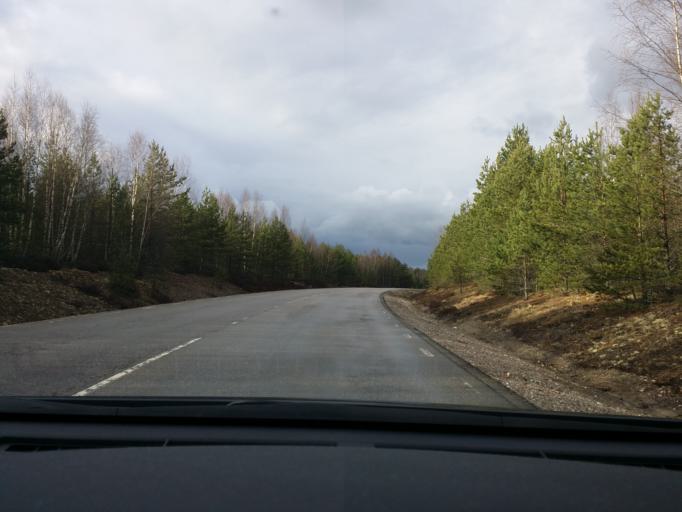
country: SE
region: Soedermanland
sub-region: Eskilstuna Kommun
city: Arla
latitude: 59.3212
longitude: 16.6797
